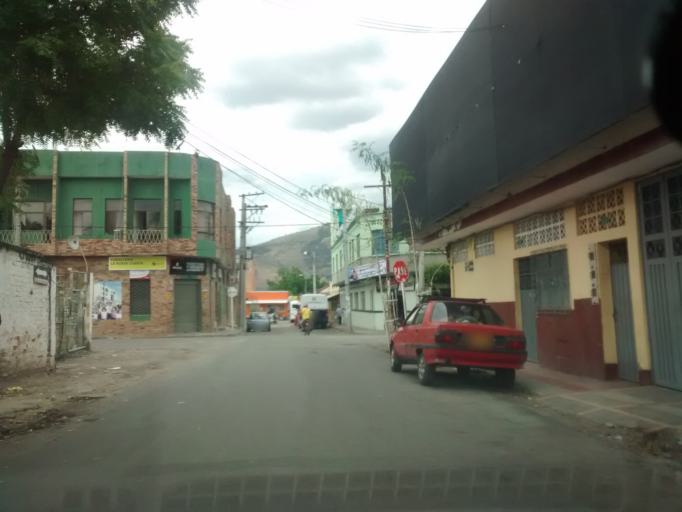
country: CO
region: Cundinamarca
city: Tocaima
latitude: 4.4583
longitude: -74.6358
